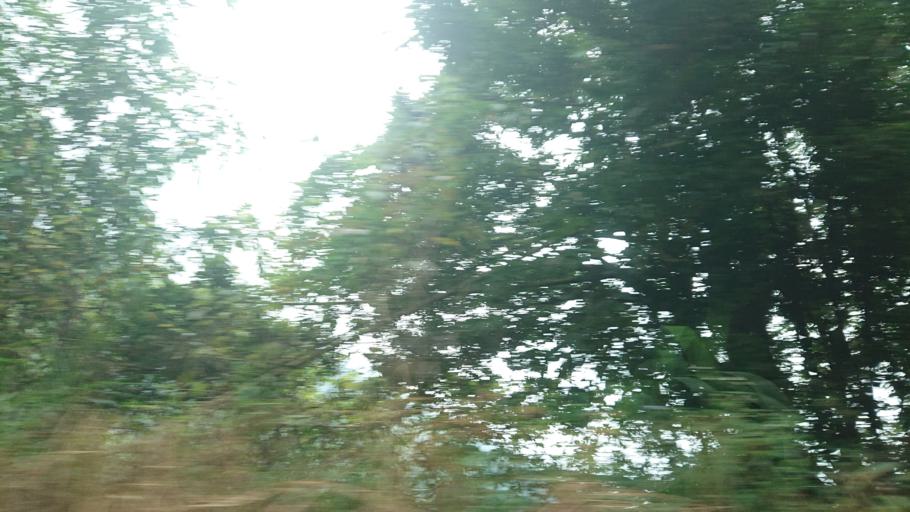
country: TW
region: Taiwan
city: Lugu
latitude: 23.6116
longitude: 120.7163
